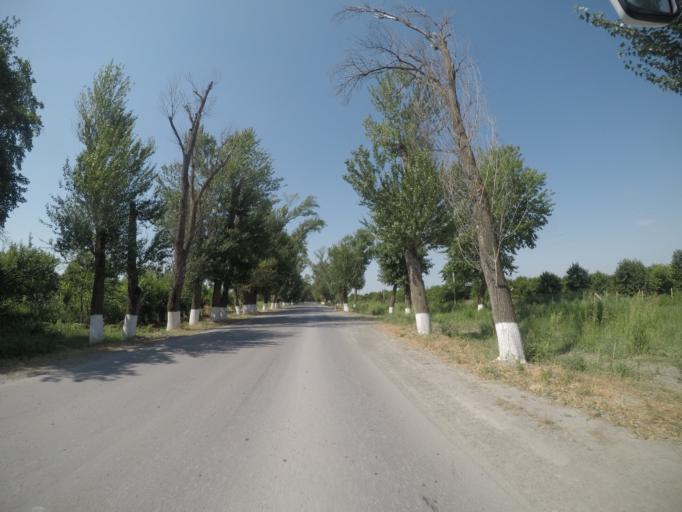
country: AZ
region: Agdas
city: Agdas
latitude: 40.6924
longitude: 47.5379
